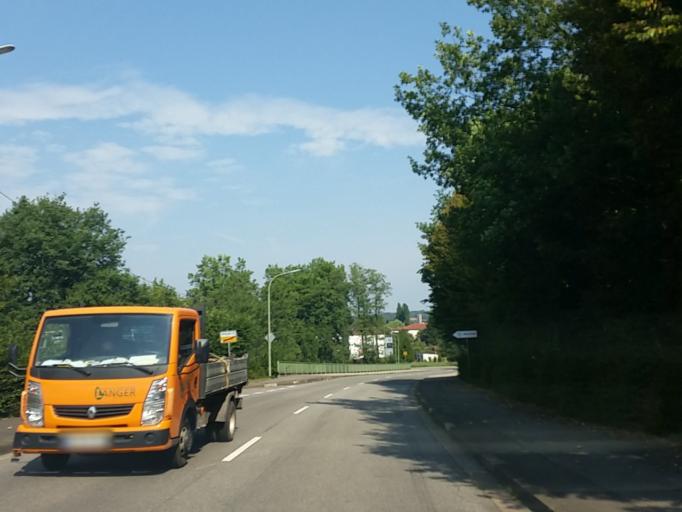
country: DE
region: Saarland
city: Schmelz
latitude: 49.4131
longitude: 6.8527
